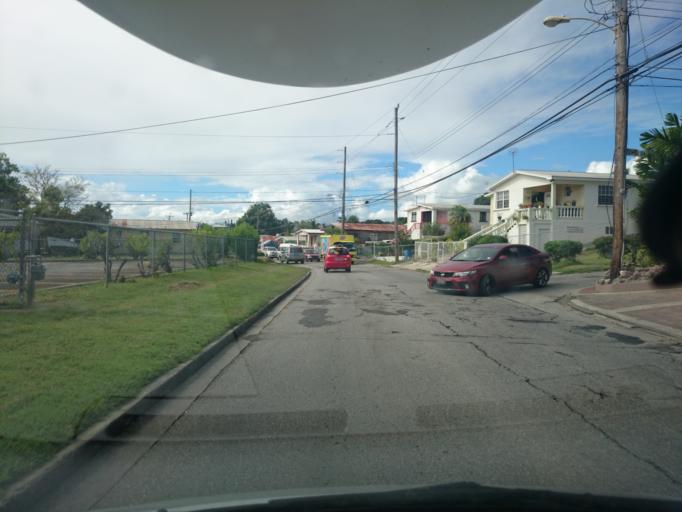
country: BB
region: Christ Church
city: Oistins
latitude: 13.0614
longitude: -59.5374
